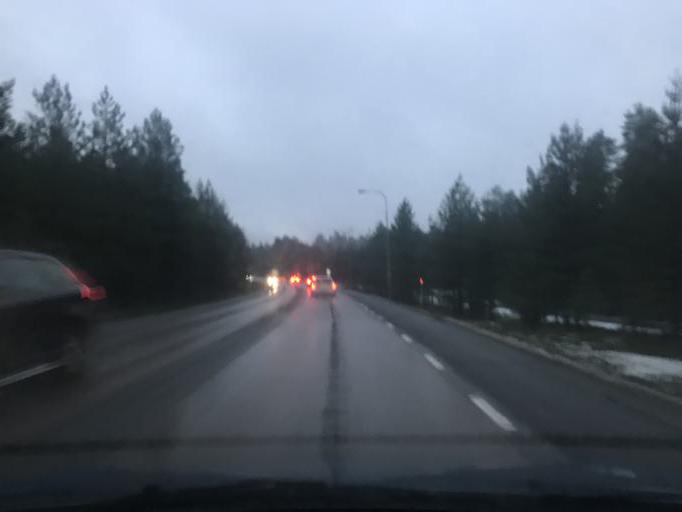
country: SE
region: Norrbotten
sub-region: Lulea Kommun
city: Gammelstad
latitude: 65.6218
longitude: 22.0354
